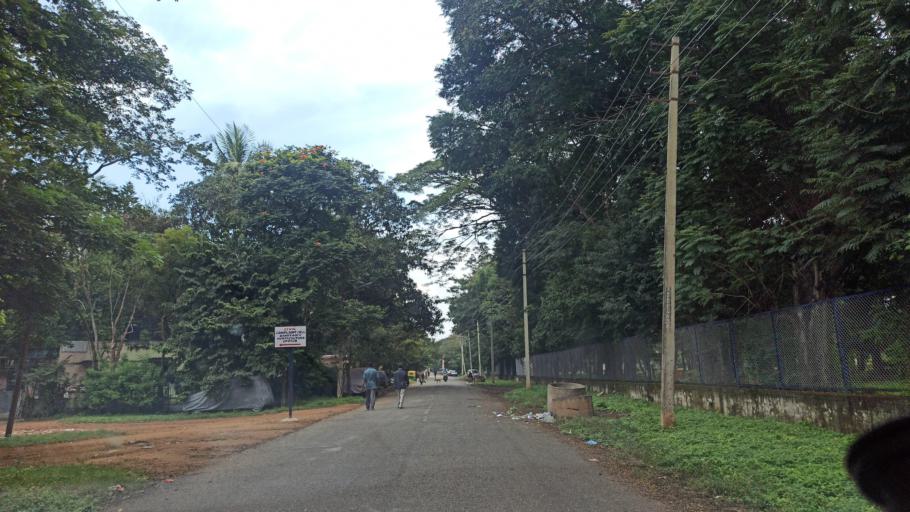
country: IN
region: Karnataka
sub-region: Bangalore Urban
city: Bangalore
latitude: 13.0069
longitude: 77.6816
